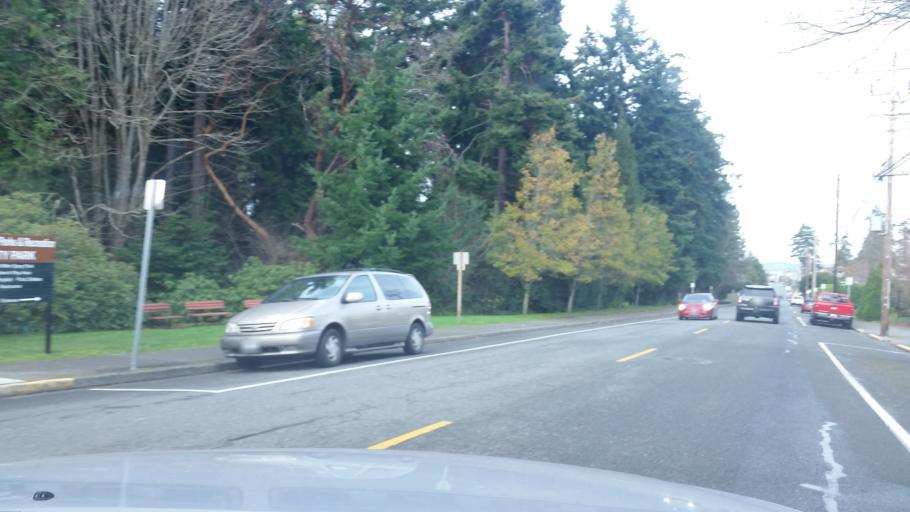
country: US
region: Washington
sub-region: Snohomish County
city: Woodway
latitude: 47.8033
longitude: -122.3802
